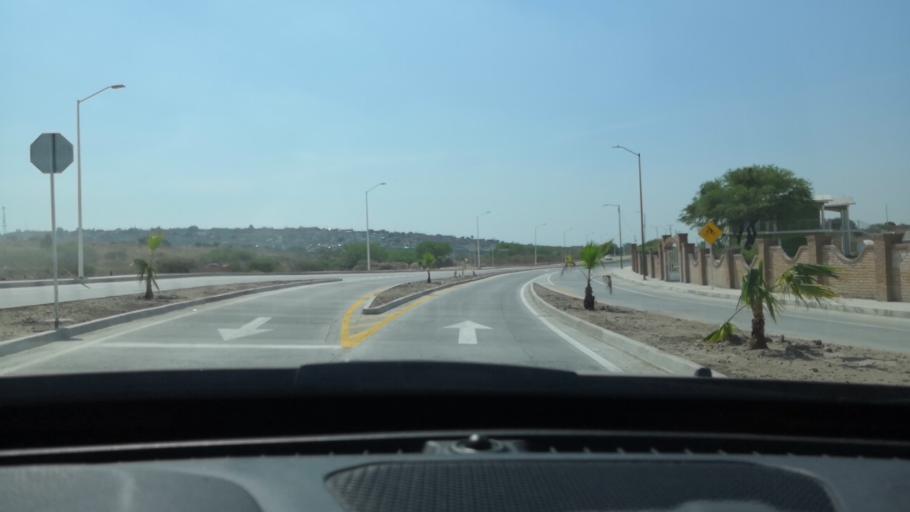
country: MX
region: Guanajuato
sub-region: Purisima del Rincon
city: Potrerillos (Guanajal)
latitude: 21.0588
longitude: -101.8681
